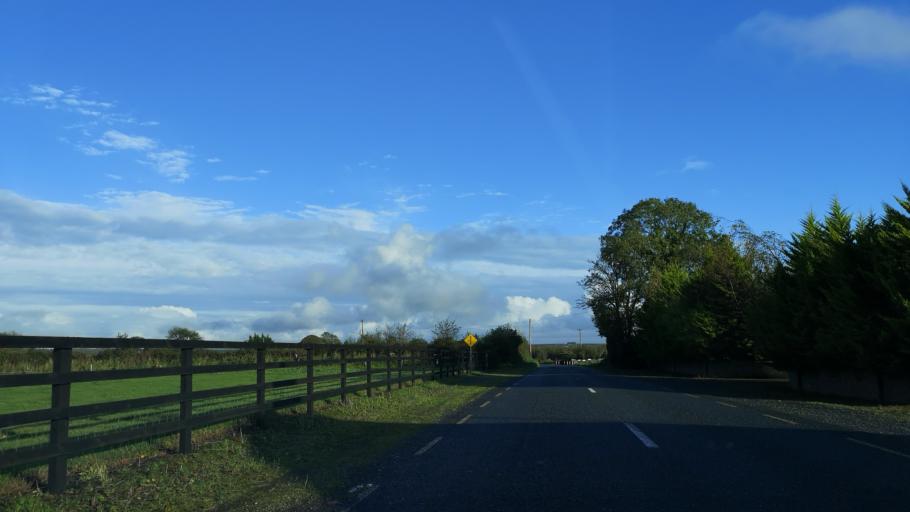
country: IE
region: Connaught
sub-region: Roscommon
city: Castlerea
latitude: 53.8071
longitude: -8.5116
